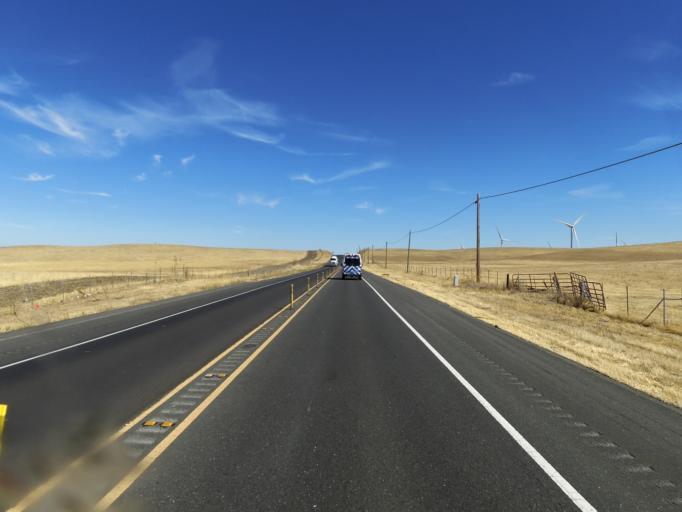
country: US
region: California
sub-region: Solano County
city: Rio Vista
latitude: 38.1837
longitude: -121.8327
